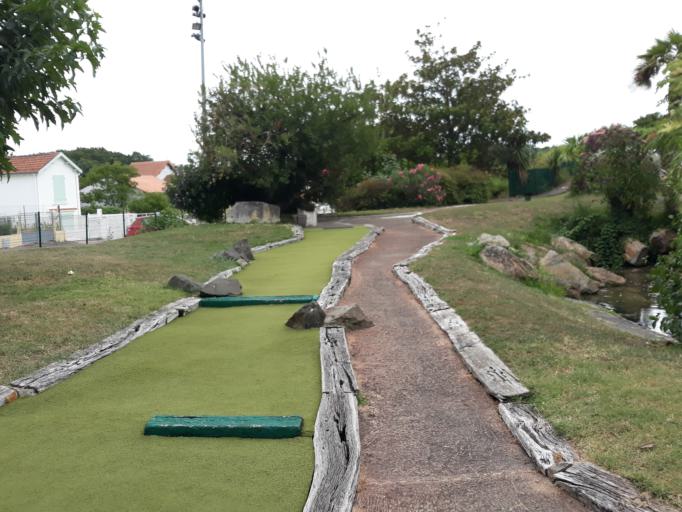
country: FR
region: Poitou-Charentes
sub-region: Departement de la Charente-Maritime
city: Fouras
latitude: 45.9925
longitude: -1.0849
